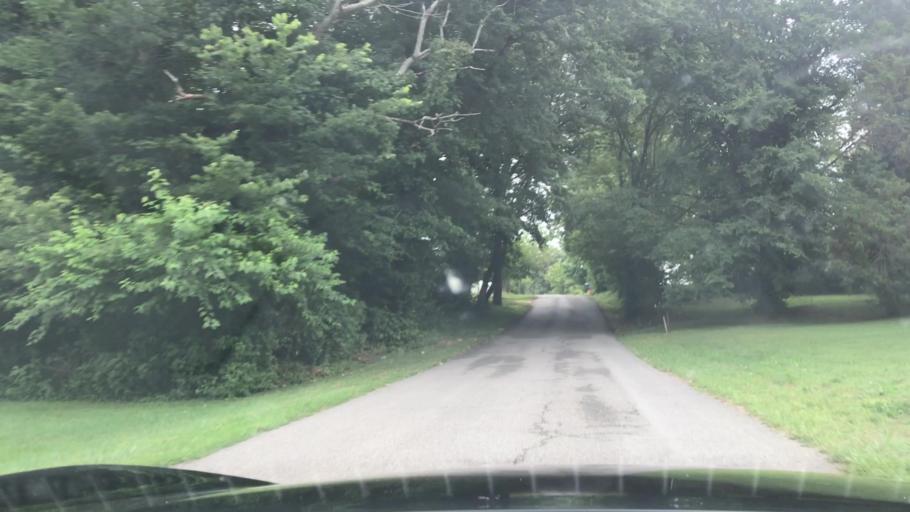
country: US
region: Kentucky
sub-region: Muhlenberg County
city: Central City
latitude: 37.2158
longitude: -87.0492
